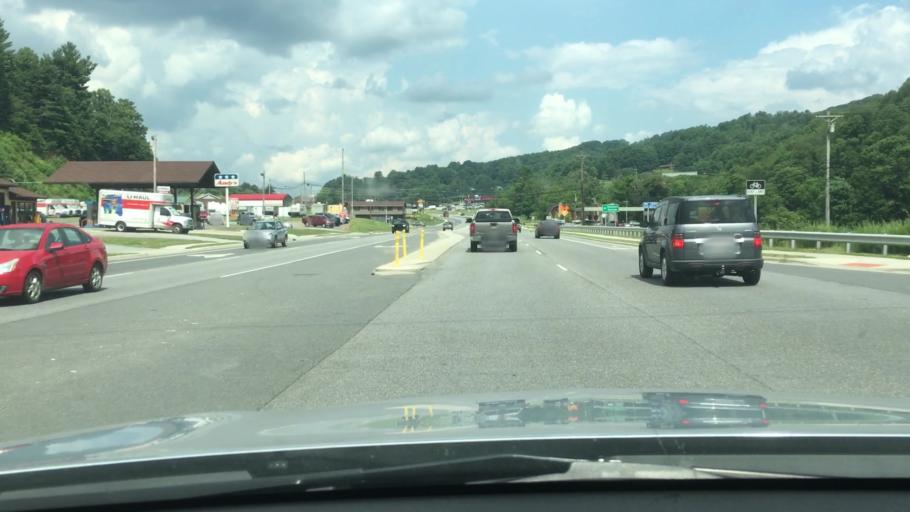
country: US
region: North Carolina
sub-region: Yancey County
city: Burnsville
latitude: 35.9124
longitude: -82.3179
